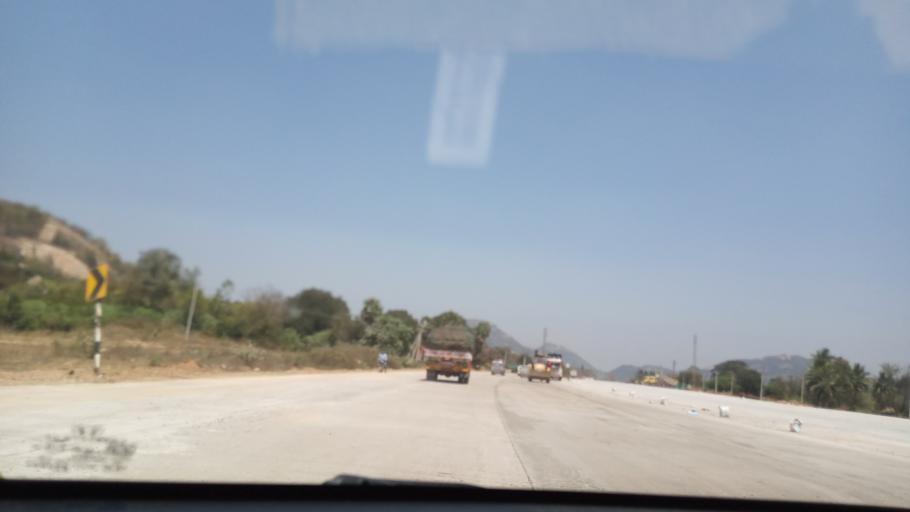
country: IN
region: Andhra Pradesh
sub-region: Chittoor
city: Pakala
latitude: 13.4787
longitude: 79.1884
